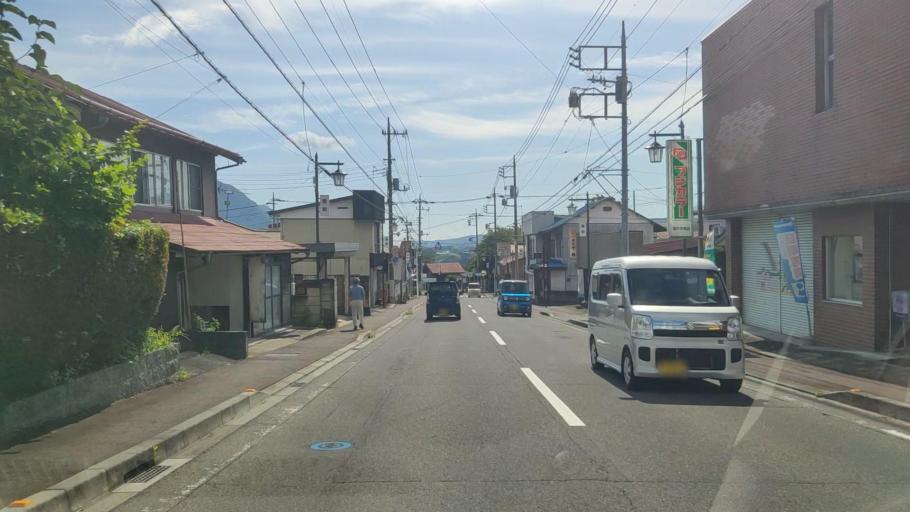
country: JP
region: Gunma
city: Nakanojomachi
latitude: 36.5883
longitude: 138.8456
